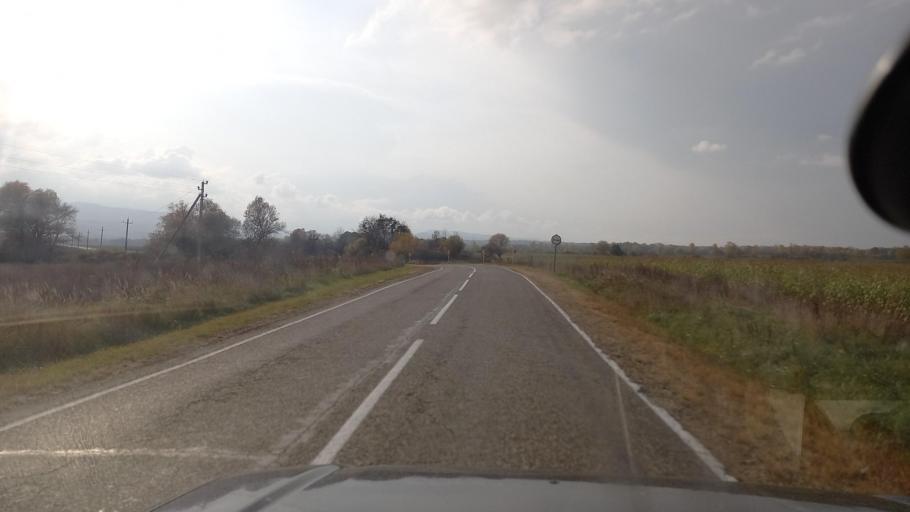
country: RU
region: Krasnodarskiy
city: Gubskaya
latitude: 44.3153
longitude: 40.5785
